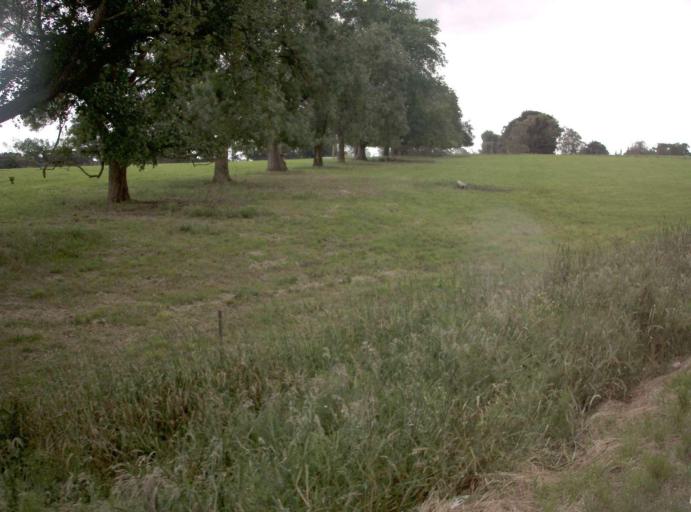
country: AU
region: Victoria
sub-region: Baw Baw
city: Warragul
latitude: -38.1053
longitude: 145.9739
